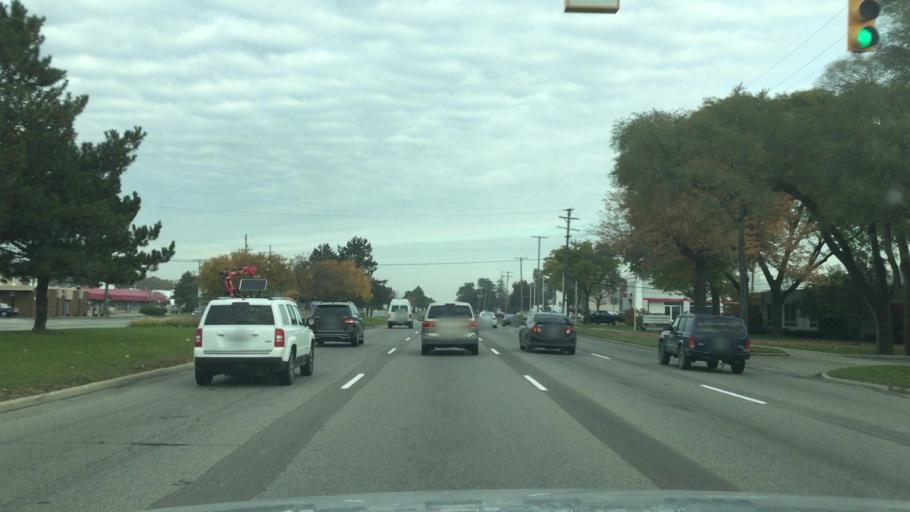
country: US
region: Michigan
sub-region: Oakland County
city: Southfield
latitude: 42.4459
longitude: -83.2779
